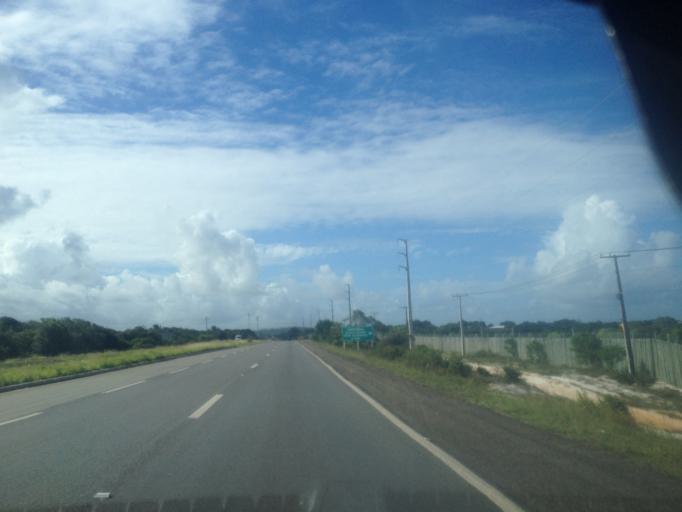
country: BR
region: Bahia
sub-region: Mata De Sao Joao
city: Mata de Sao Joao
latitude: -12.6164
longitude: -38.0557
